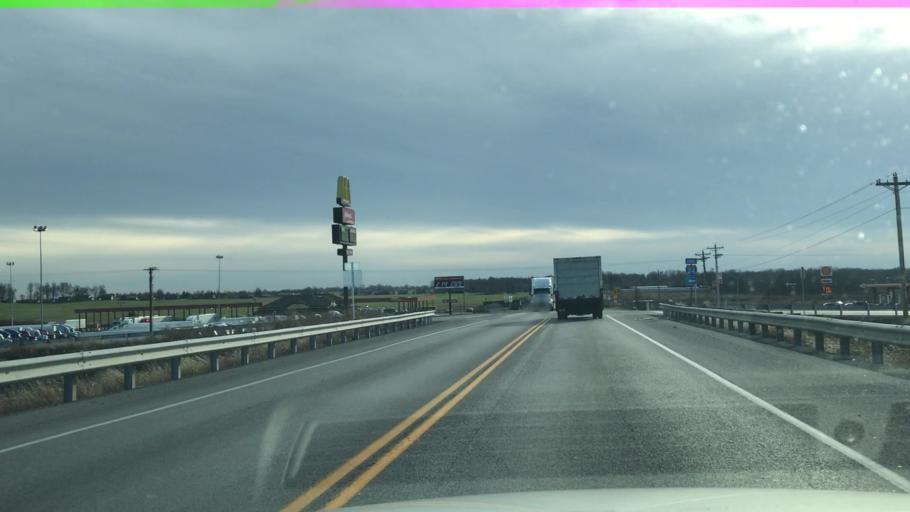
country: US
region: Kentucky
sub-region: Christian County
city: Oak Grove
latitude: 36.6810
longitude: -87.4048
